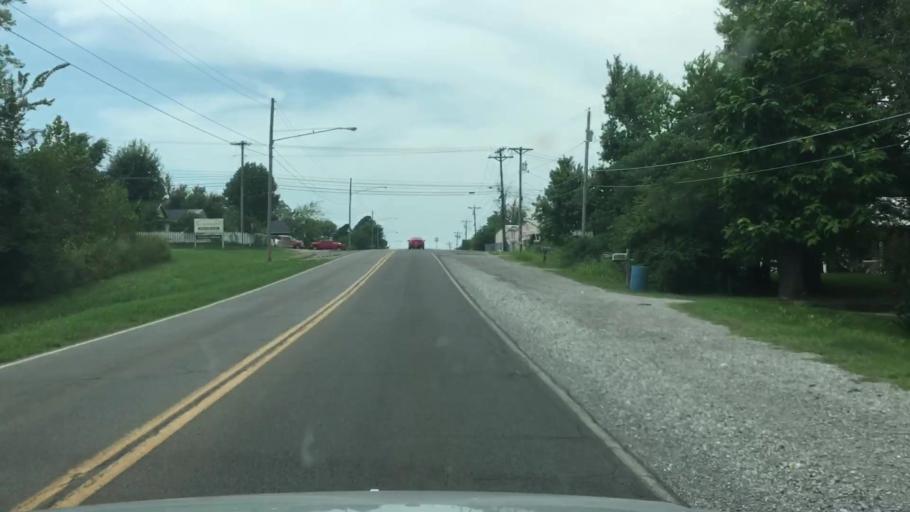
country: US
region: Oklahoma
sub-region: Cherokee County
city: Tahlequah
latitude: 35.9163
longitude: -94.9882
